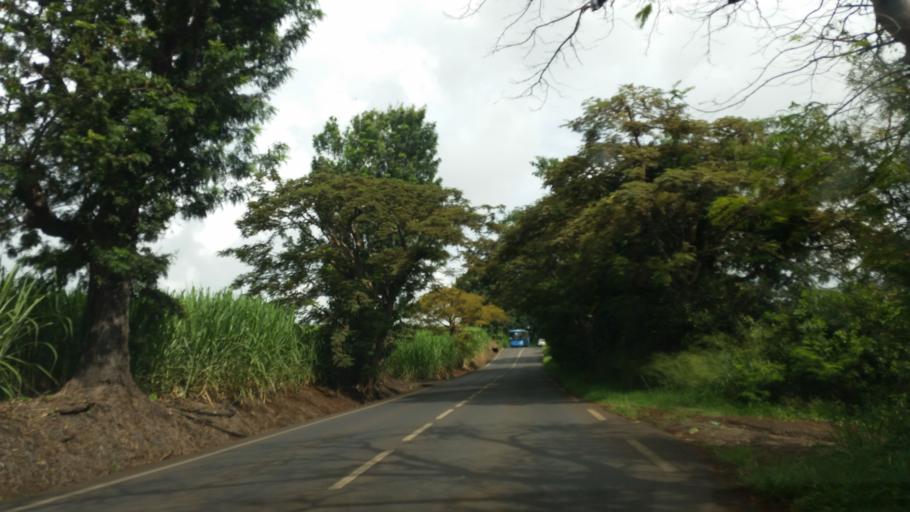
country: RE
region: Reunion
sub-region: Reunion
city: Trois-Bassins
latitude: -21.0622
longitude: 55.2666
